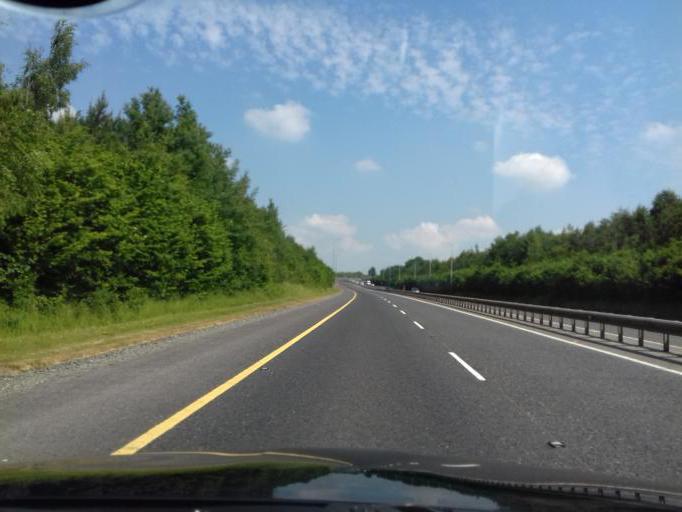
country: IE
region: Leinster
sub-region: An Mhi
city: Ashbourne
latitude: 53.5186
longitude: -6.4198
